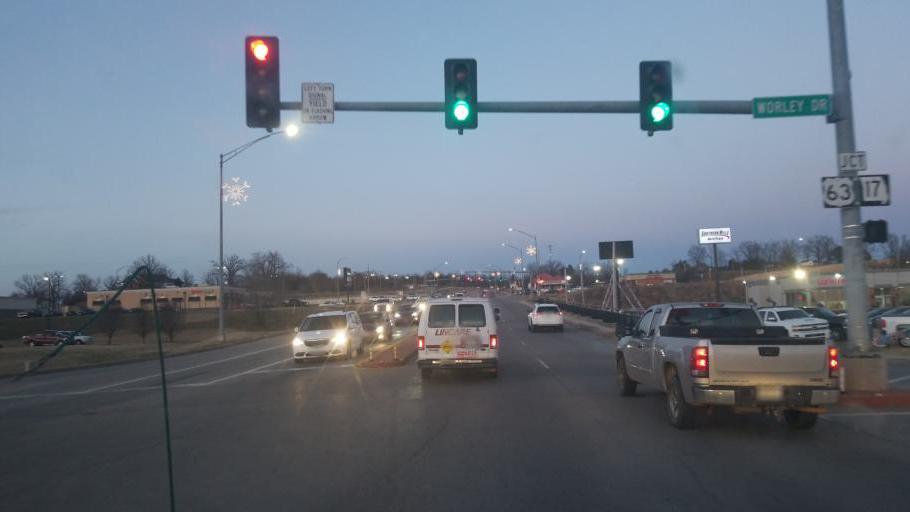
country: US
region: Missouri
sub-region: Howell County
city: West Plains
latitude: 36.7161
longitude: -91.8736
